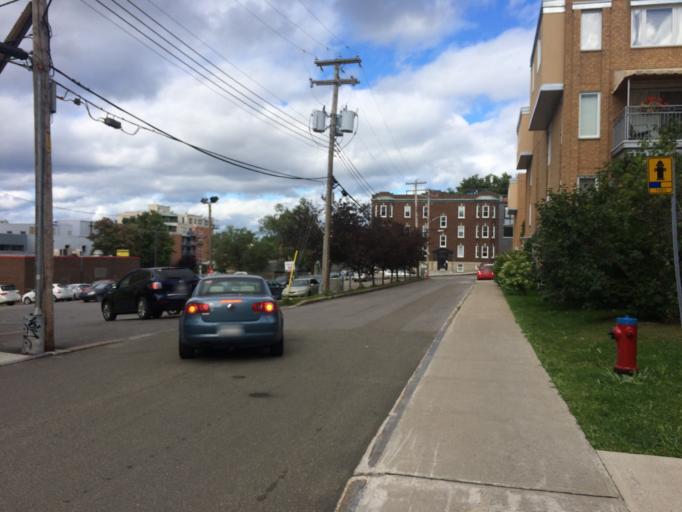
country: CA
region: Quebec
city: Quebec
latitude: 46.8038
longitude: -71.2307
